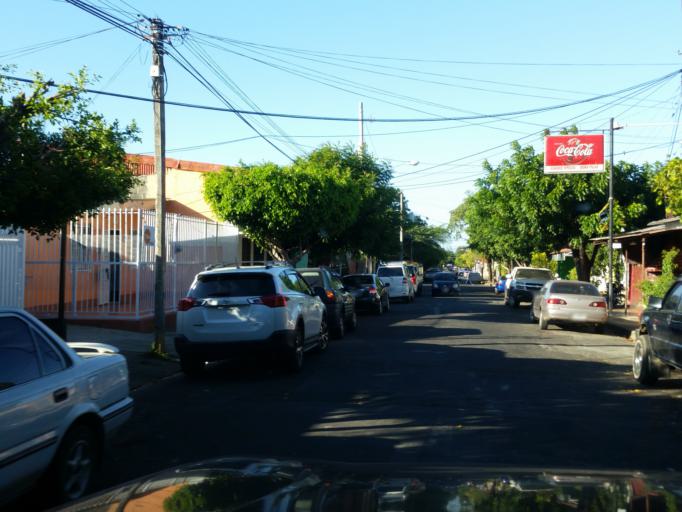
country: NI
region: Managua
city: Managua
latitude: 12.1441
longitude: -86.2814
